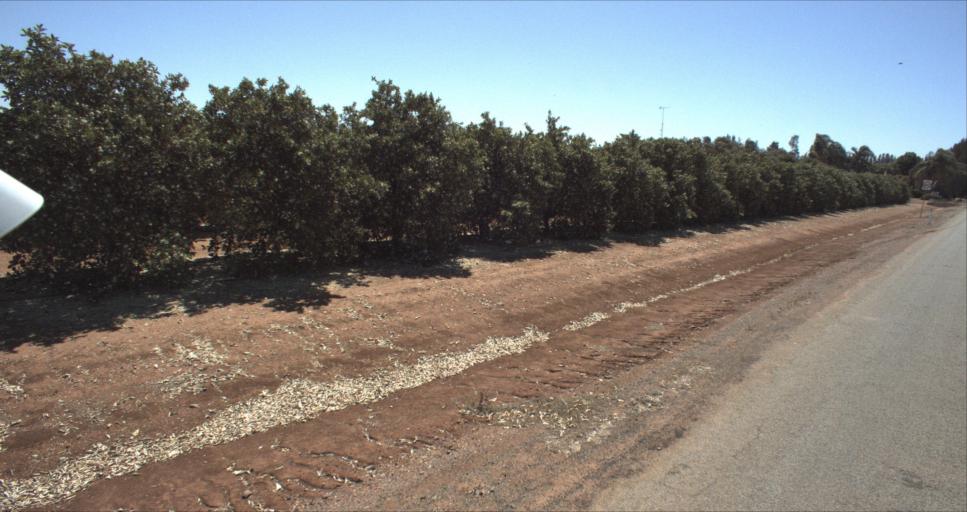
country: AU
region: New South Wales
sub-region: Leeton
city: Leeton
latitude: -34.5321
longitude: 146.3288
